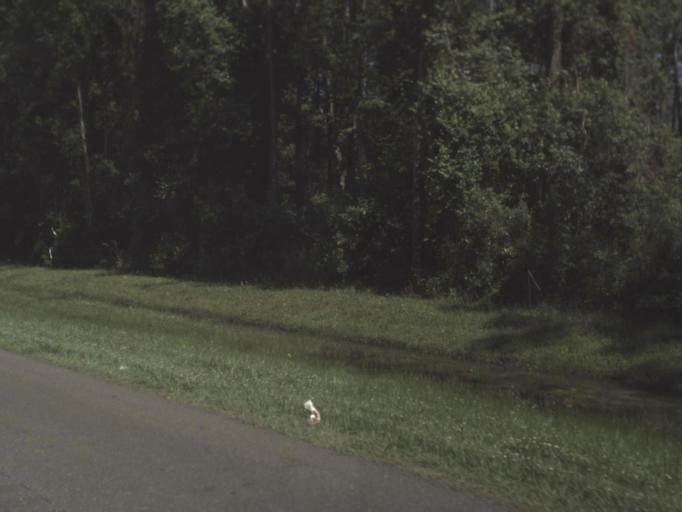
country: US
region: Florida
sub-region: Duval County
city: Baldwin
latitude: 30.3058
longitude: -81.8851
